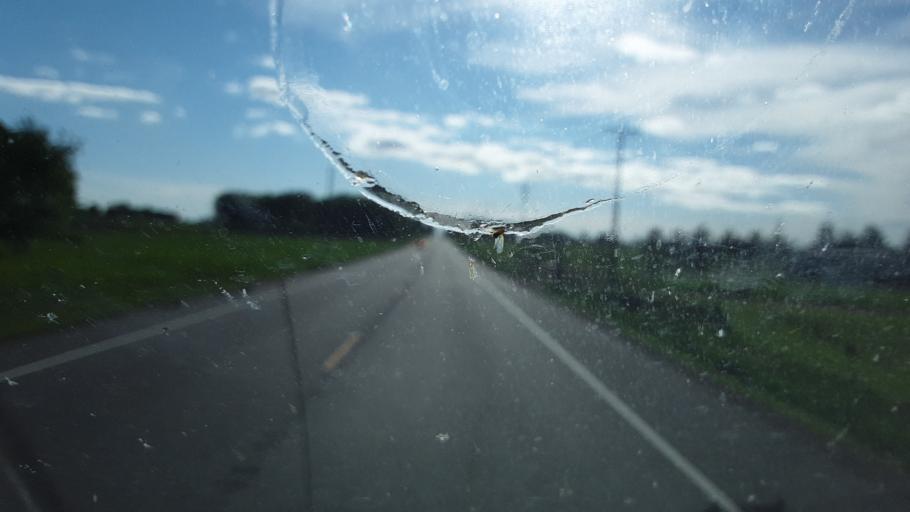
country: US
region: Wisconsin
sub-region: Wood County
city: Marshfield
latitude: 44.6564
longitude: -90.2689
